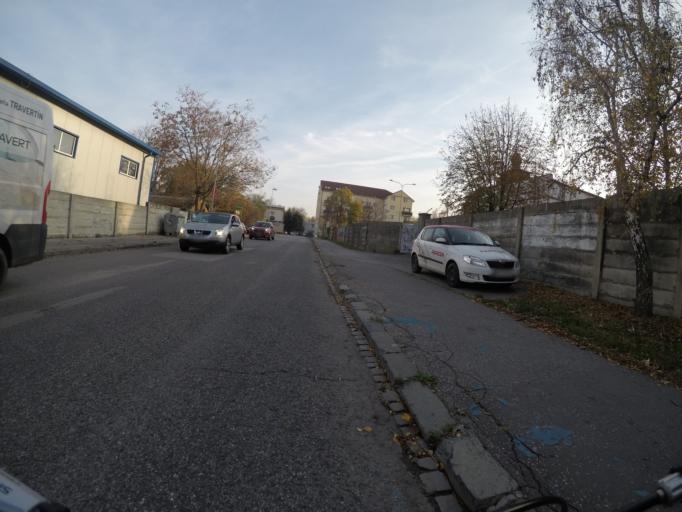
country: SK
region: Bratislavsky
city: Bratislava
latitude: 48.1770
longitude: 17.1561
